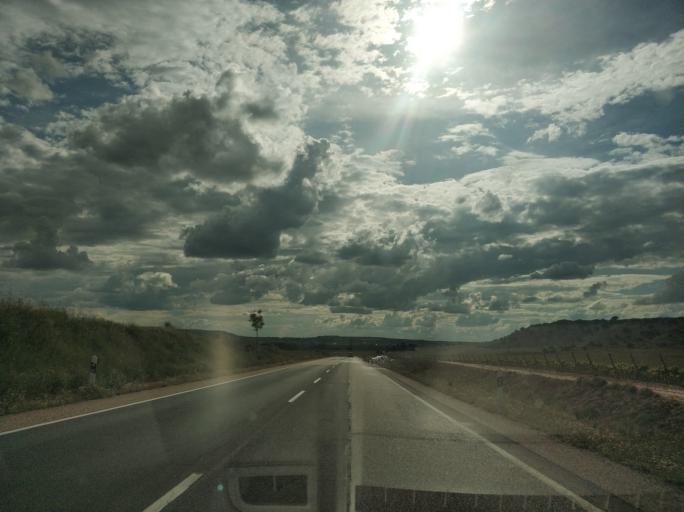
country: ES
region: Castille and Leon
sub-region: Provincia de Burgos
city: Haza
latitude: 41.6367
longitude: -3.8210
